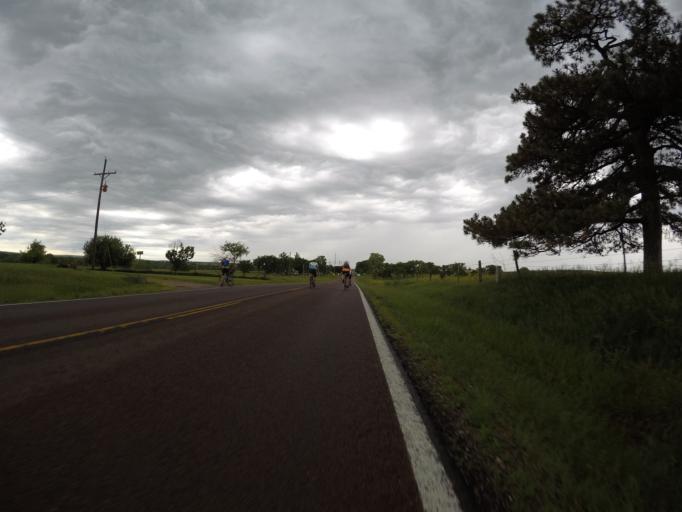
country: US
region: Kansas
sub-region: Shawnee County
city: Rossville
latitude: 38.9574
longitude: -96.0369
